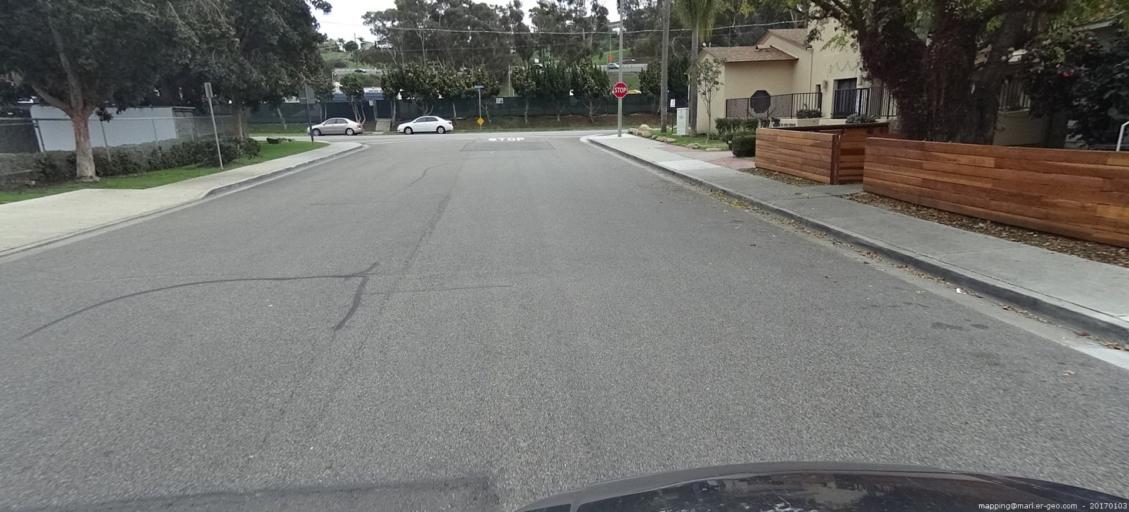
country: US
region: California
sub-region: Orange County
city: Dana Point
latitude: 33.4648
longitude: -117.6765
